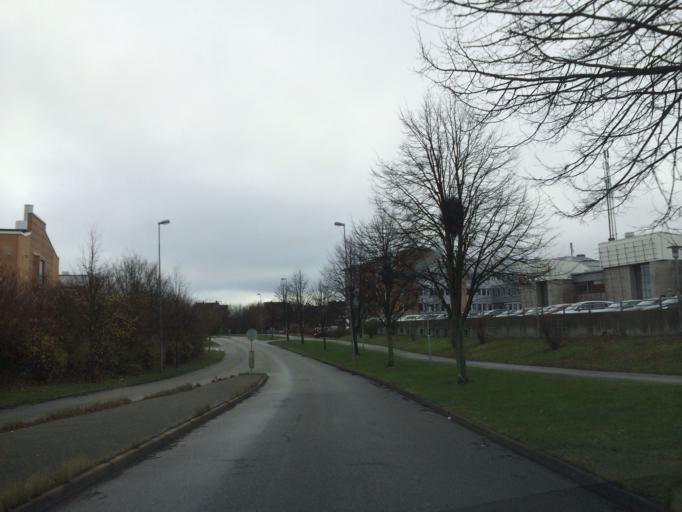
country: SE
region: Skane
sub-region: Lunds Kommun
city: Lund
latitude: 55.7130
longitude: 13.2164
